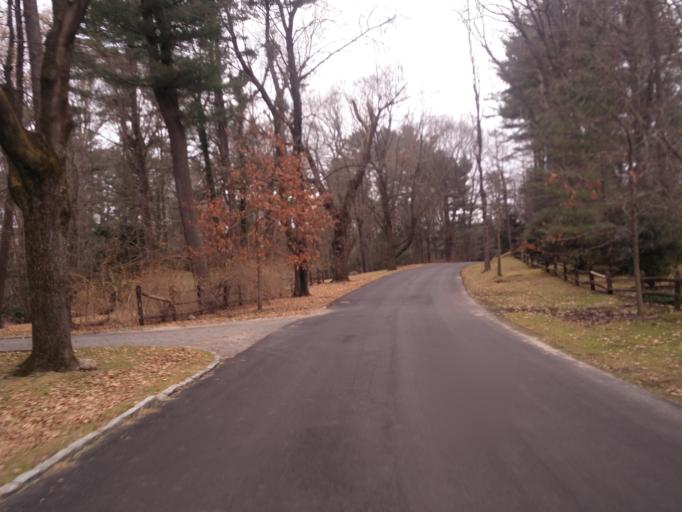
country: US
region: New York
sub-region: Nassau County
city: Locust Valley
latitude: 40.8717
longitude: -73.5996
